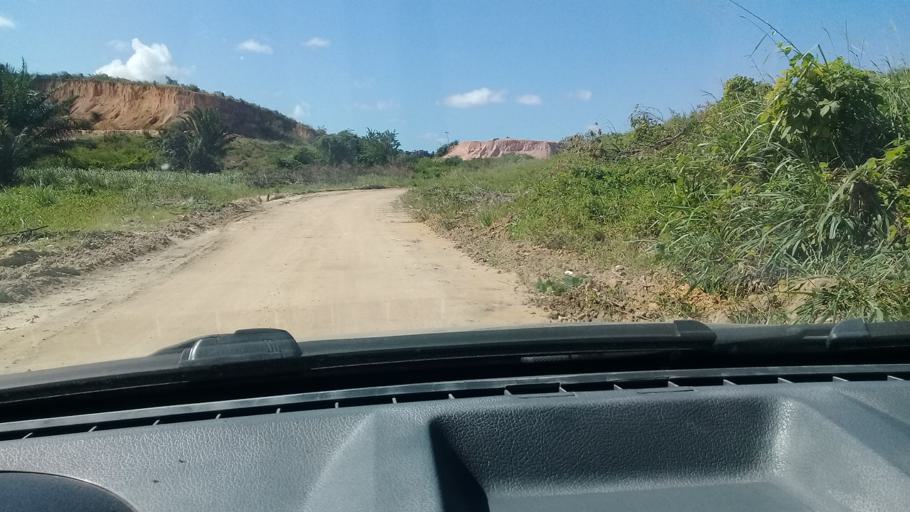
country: BR
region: Pernambuco
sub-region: Jaboatao Dos Guararapes
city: Jaboatao
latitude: -8.1501
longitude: -34.9518
